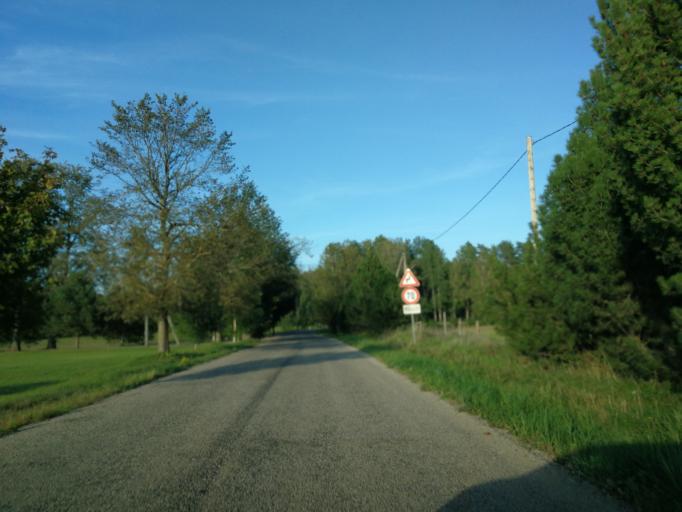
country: LV
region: Garkalne
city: Garkalne
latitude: 57.0775
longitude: 24.4511
